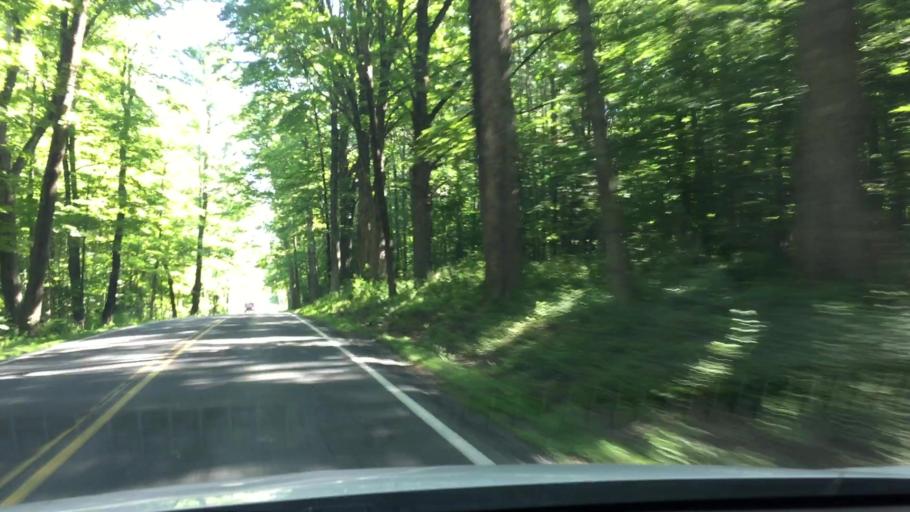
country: US
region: Massachusetts
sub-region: Berkshire County
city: Richmond
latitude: 42.3926
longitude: -73.3369
